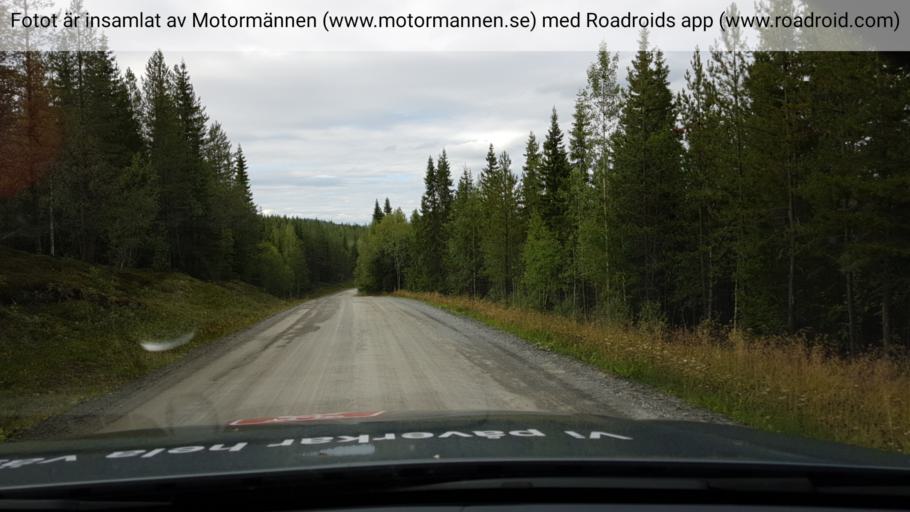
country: SE
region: Jaemtland
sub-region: Krokoms Kommun
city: Valla
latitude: 63.6728
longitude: 13.6973
